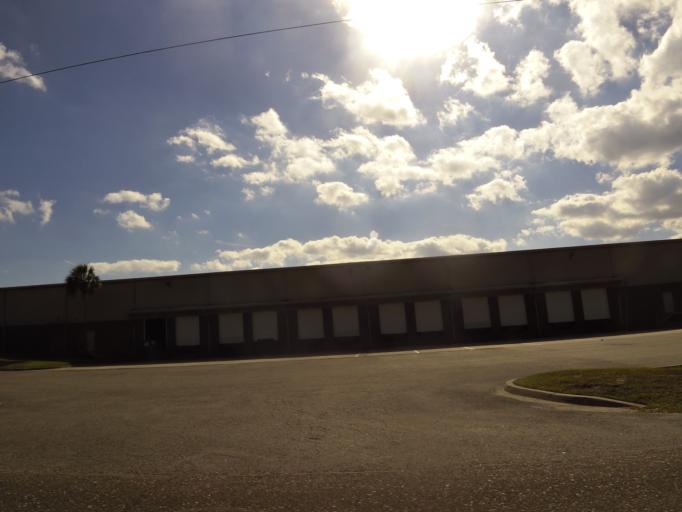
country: US
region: Florida
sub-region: Duval County
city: Jacksonville
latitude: 30.4101
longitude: -81.6383
